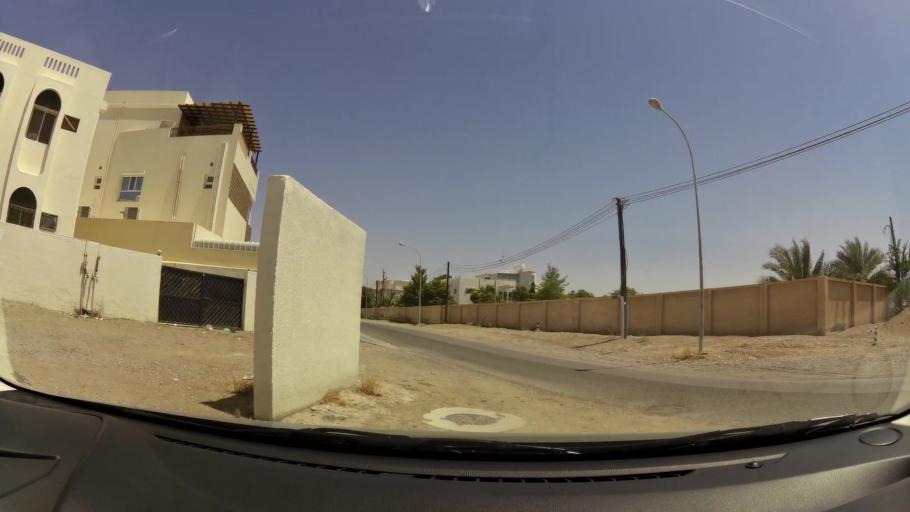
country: OM
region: Muhafazat Masqat
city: As Sib al Jadidah
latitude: 23.6188
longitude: 58.2348
